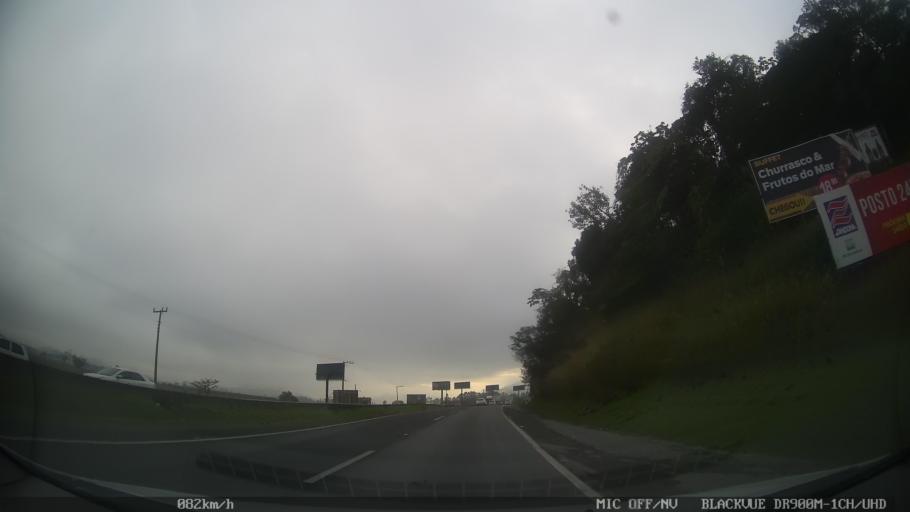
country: BR
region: Santa Catarina
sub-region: Navegantes
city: Navegantes
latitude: -26.8363
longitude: -48.7107
